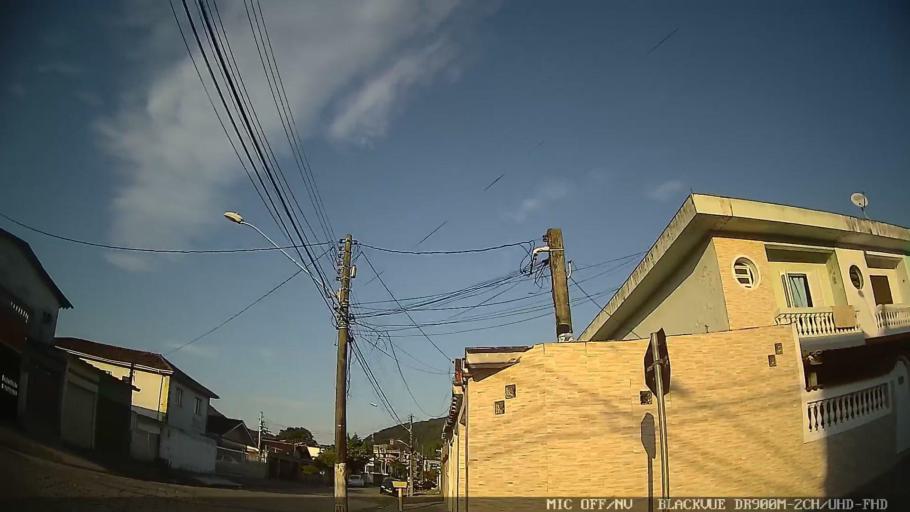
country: BR
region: Sao Paulo
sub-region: Guaruja
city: Guaruja
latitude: -23.9909
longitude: -46.2759
